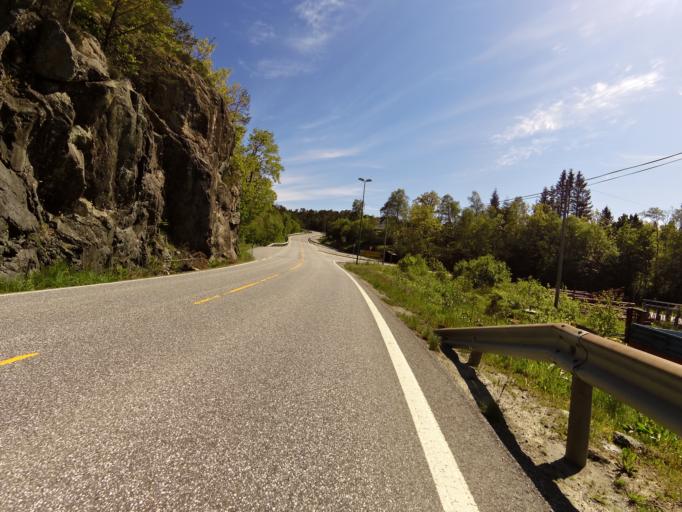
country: NO
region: Hordaland
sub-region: Stord
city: Sagvag
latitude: 59.7890
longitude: 5.3719
